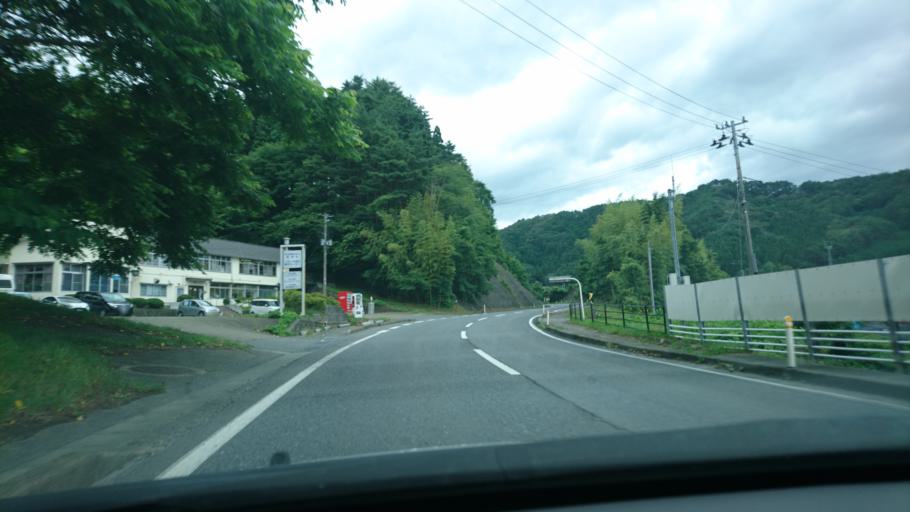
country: JP
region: Iwate
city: Kamaishi
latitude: 39.2063
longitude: 141.8647
